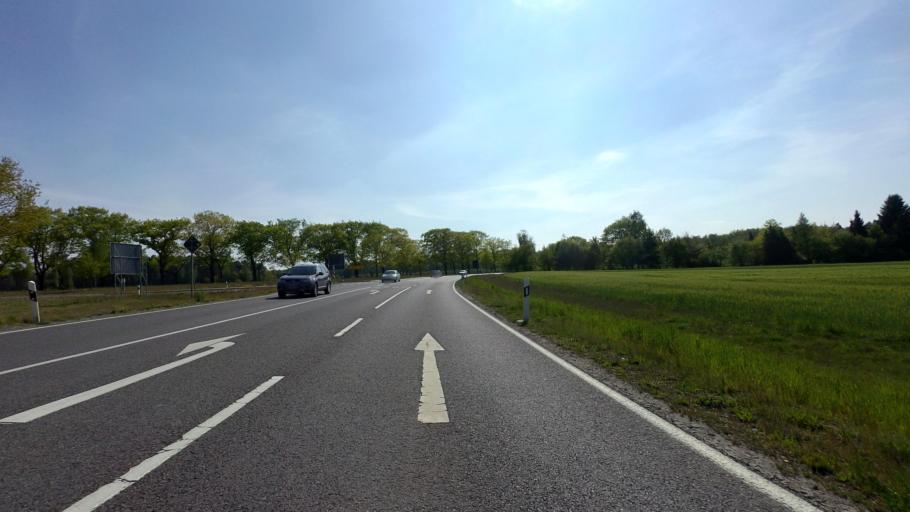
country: DE
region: Saxony
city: Wittichenau
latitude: 51.3821
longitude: 14.2225
